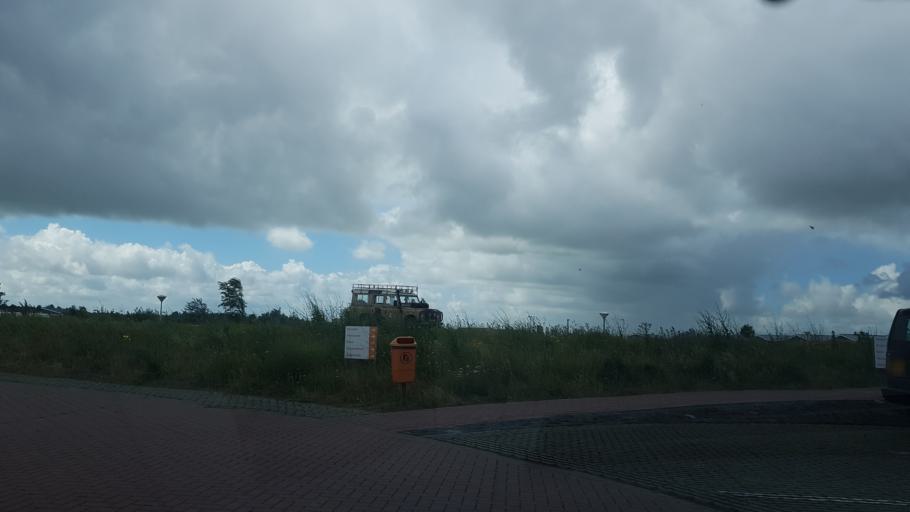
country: NL
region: Friesland
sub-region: Gemeente Dongeradeel
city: Anjum
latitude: 53.4038
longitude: 6.2119
